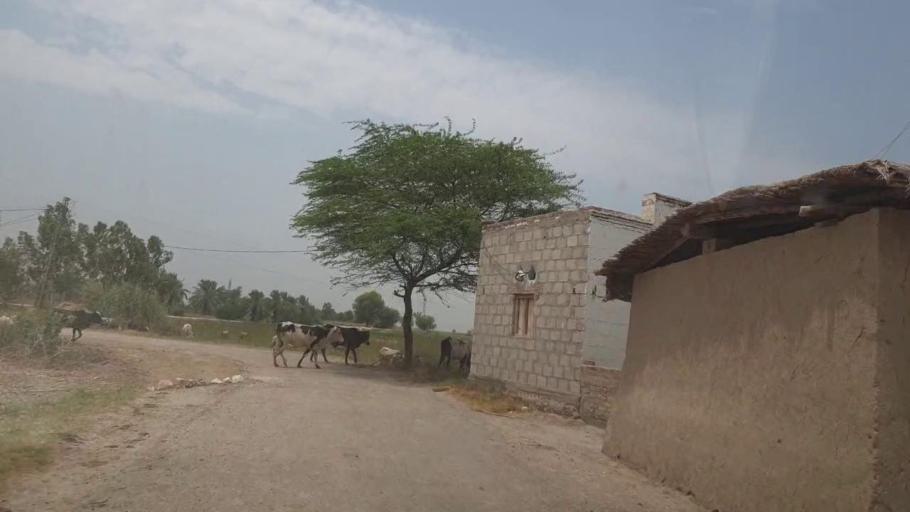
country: PK
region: Sindh
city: Kot Diji
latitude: 27.4433
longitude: 68.6791
